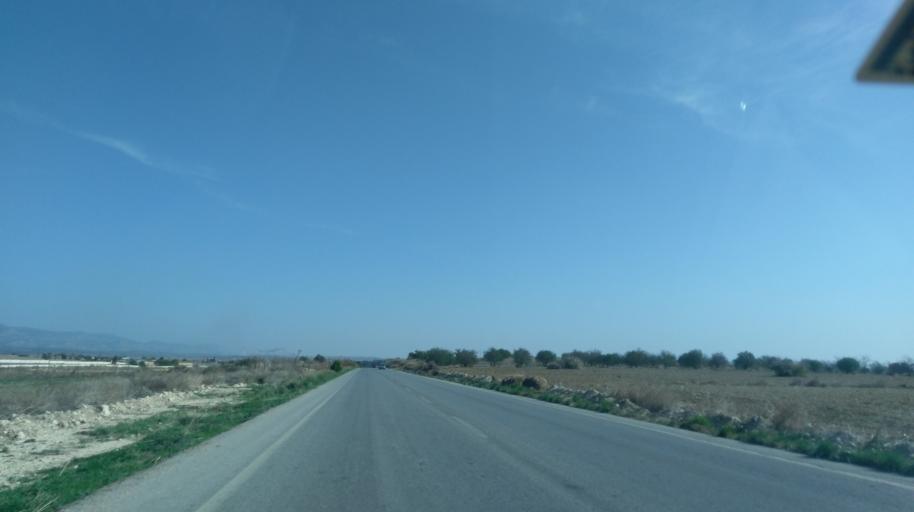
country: CY
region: Ammochostos
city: Lefkonoiko
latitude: 35.2560
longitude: 33.6376
